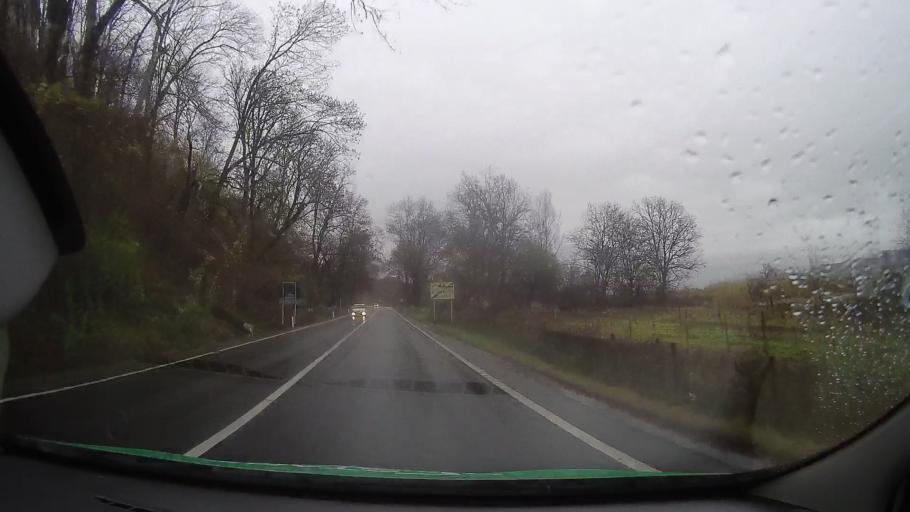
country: RO
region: Mures
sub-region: Comuna Brancovenesti
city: Brancovenesti
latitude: 46.8613
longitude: 24.7682
